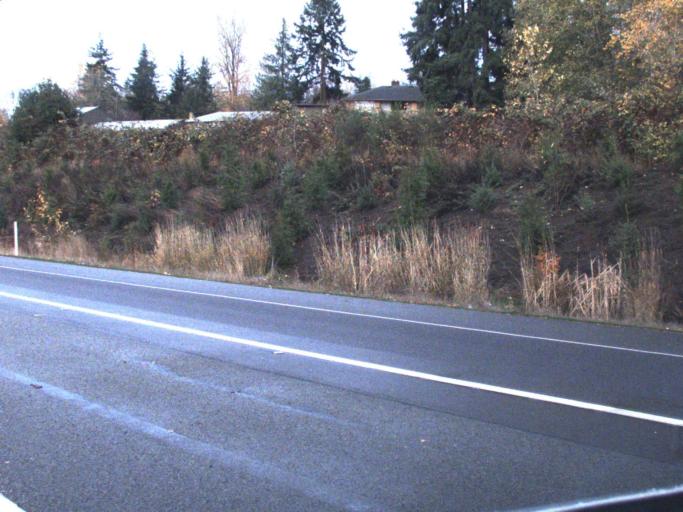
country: US
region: Washington
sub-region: Snohomish County
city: Fobes Hill
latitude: 47.9656
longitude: -122.1283
